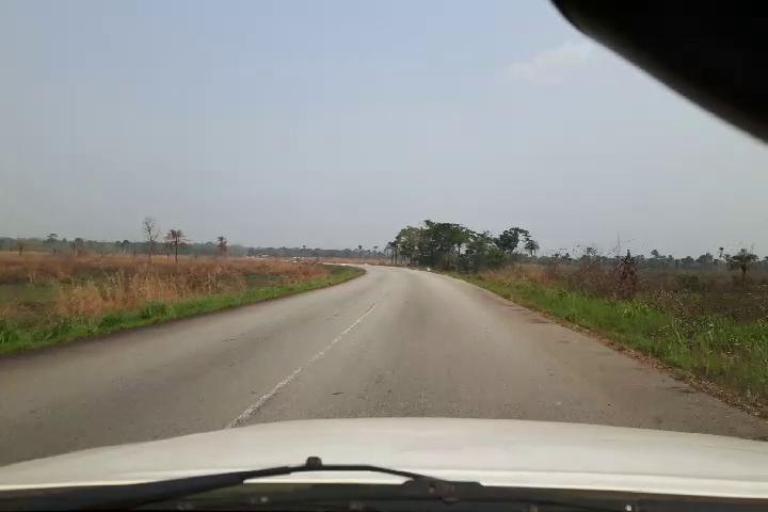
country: SL
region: Southern Province
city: Baiima
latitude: 8.1485
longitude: -11.9066
